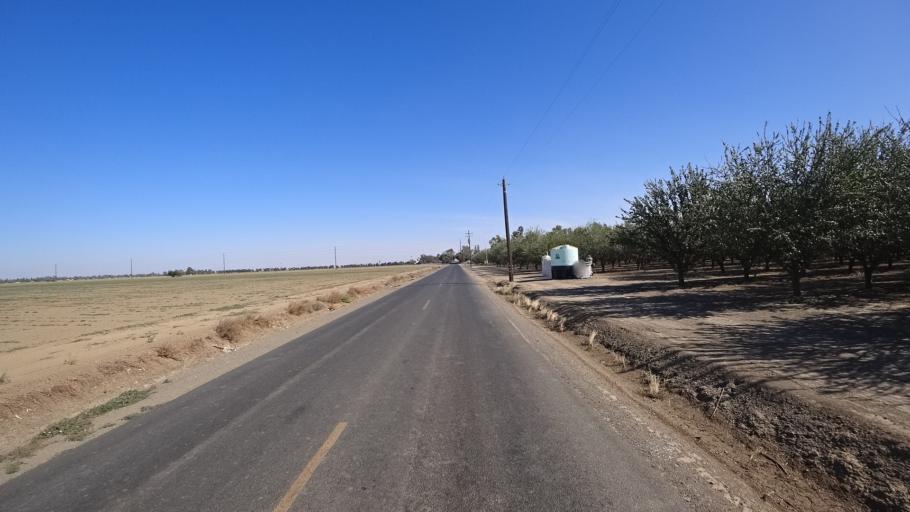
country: US
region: California
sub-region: Yolo County
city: Woodland
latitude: 38.6413
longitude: -121.7976
